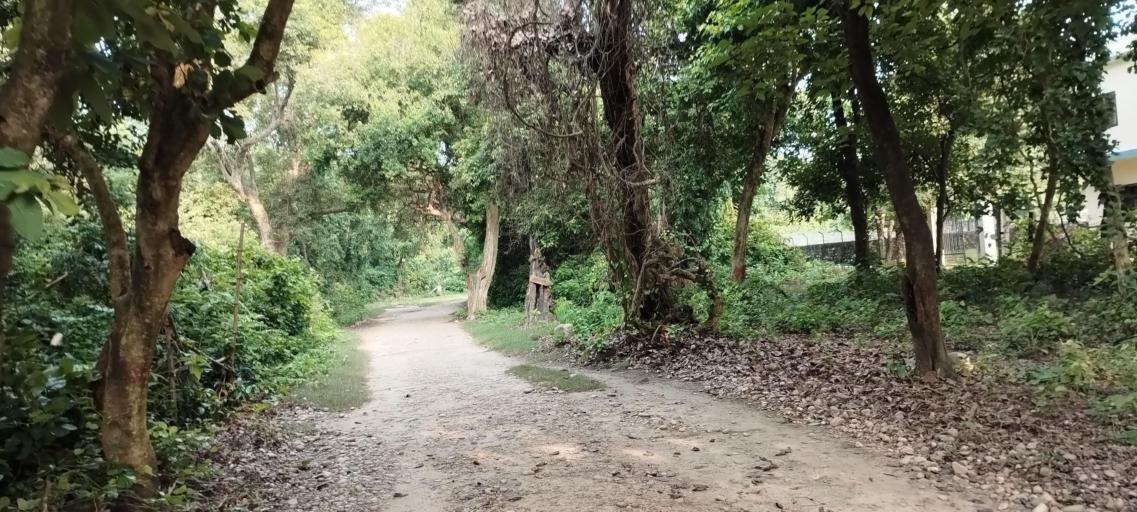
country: NP
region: Far Western
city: Tikapur
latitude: 28.4529
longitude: 81.2420
